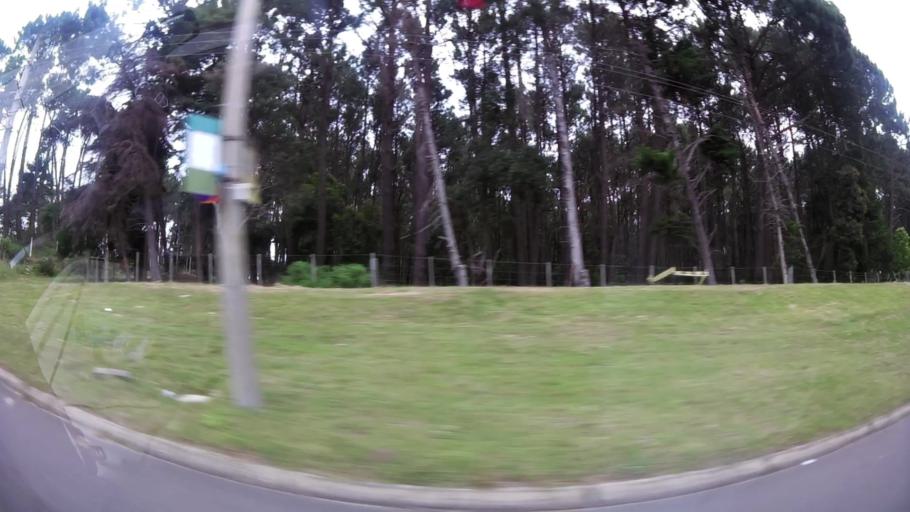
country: UY
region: Maldonado
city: Maldonado
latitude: -34.9053
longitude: -55.0237
